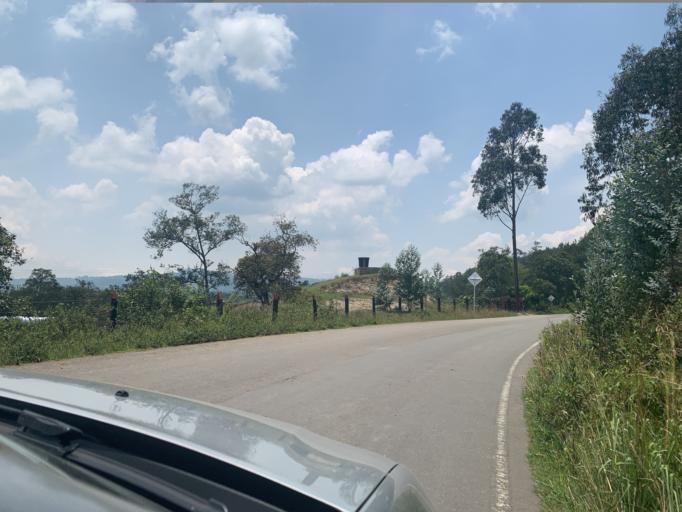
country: CO
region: Boyaca
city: Chiquinquira
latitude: 5.5431
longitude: -73.7505
